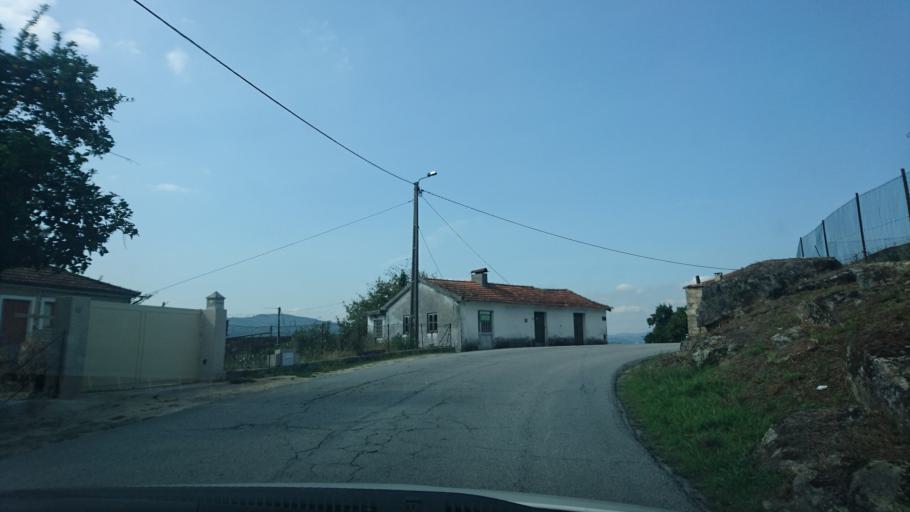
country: PT
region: Vila Real
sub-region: Mondim de Basto
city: Mondim de Basto
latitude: 41.4453
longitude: -7.9259
